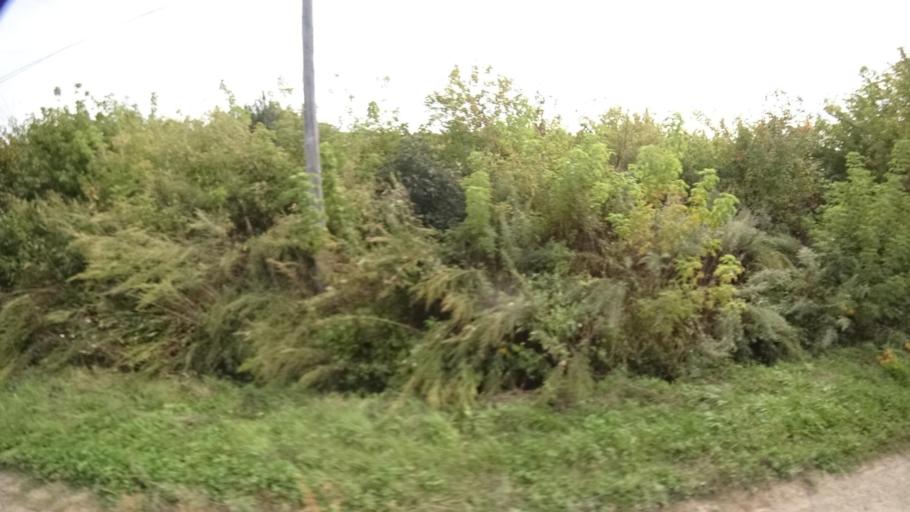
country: RU
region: Primorskiy
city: Dostoyevka
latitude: 44.3283
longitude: 133.4862
